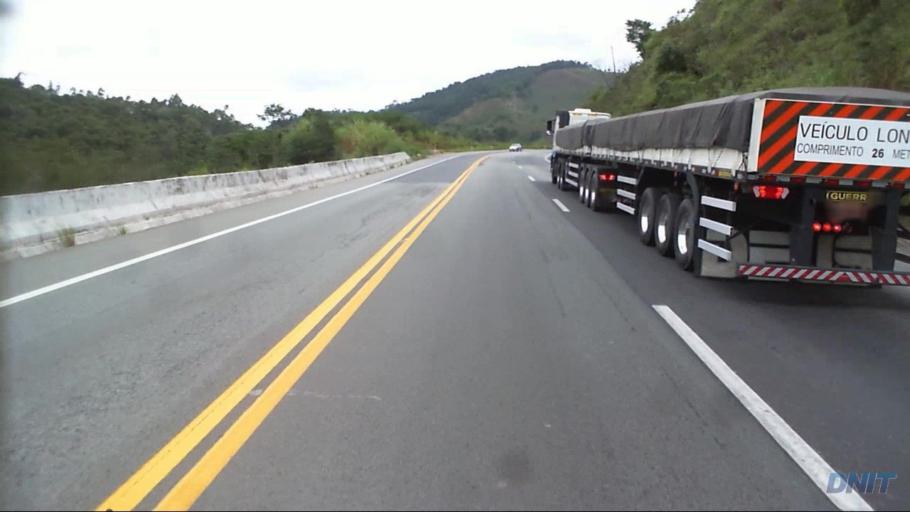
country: BR
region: Minas Gerais
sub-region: Nova Era
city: Nova Era
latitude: -19.6331
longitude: -42.8886
